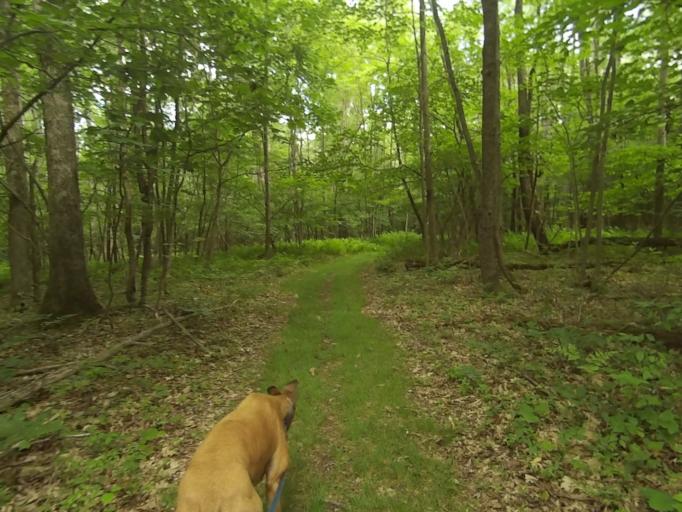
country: US
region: Pennsylvania
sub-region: Centre County
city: Stormstown
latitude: 40.9174
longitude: -78.0726
